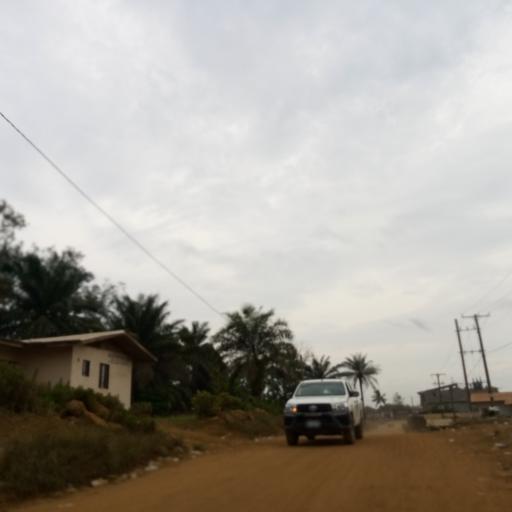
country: LR
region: Montserrado
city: Monrovia
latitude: 6.2962
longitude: -10.6804
